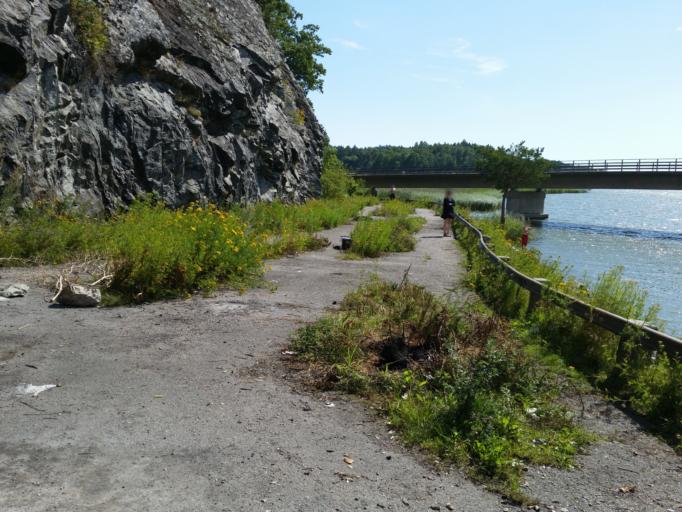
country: SE
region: Soedermanland
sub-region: Trosa Kommun
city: Vagnharad
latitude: 58.9901
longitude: 17.6224
